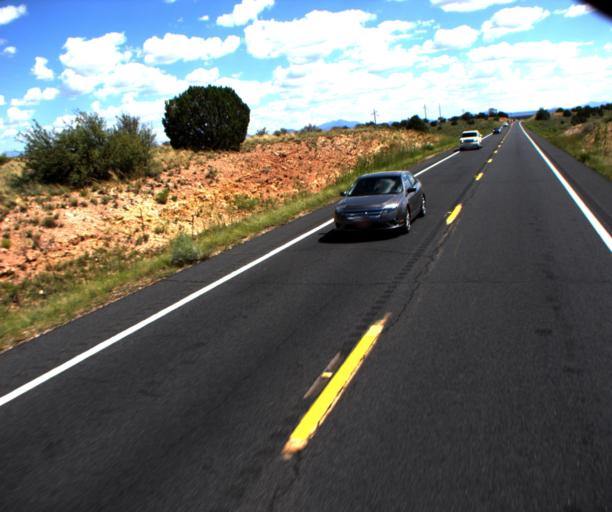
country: US
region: Arizona
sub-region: Coconino County
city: Grand Canyon Village
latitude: 35.7169
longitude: -112.1312
